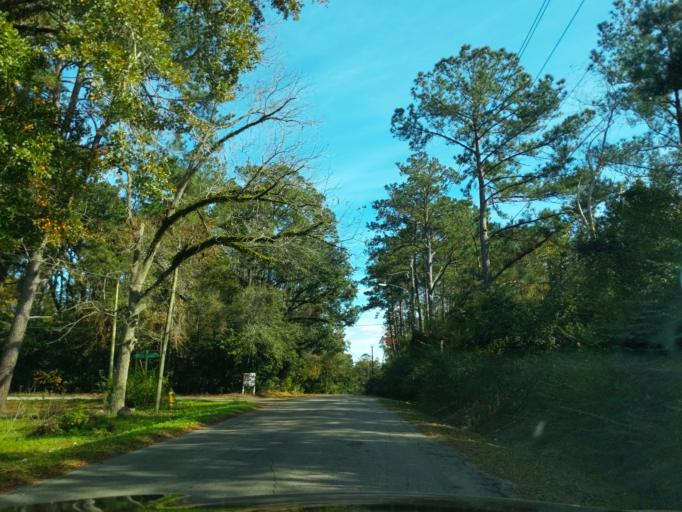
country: US
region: Florida
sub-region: Leon County
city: Tallahassee
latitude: 30.4695
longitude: -84.3411
